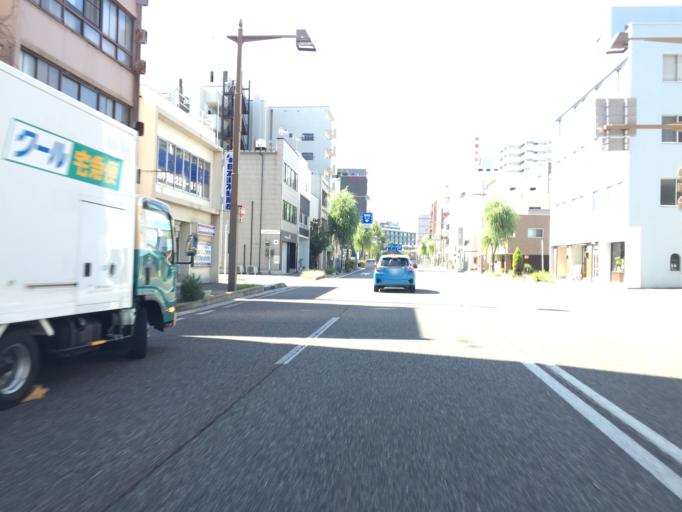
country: JP
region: Niigata
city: Niigata-shi
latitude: 37.9186
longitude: 139.0386
